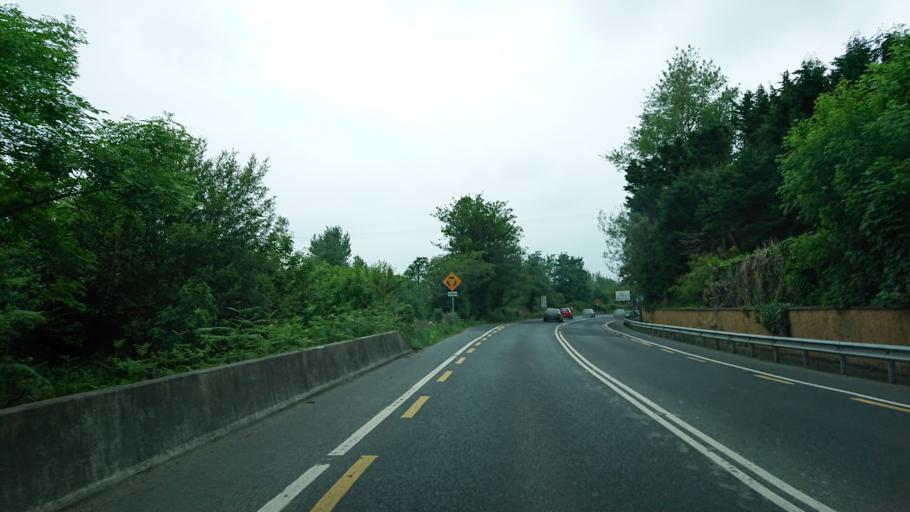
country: IE
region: Munster
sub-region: Waterford
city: Waterford
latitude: 52.2219
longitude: -7.1279
